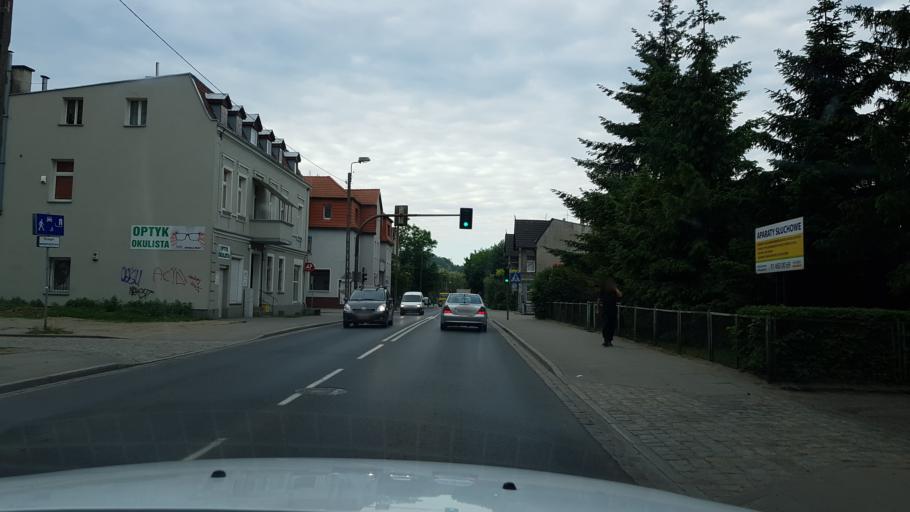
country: PL
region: West Pomeranian Voivodeship
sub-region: Szczecin
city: Szczecin
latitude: 53.3816
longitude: 14.6307
